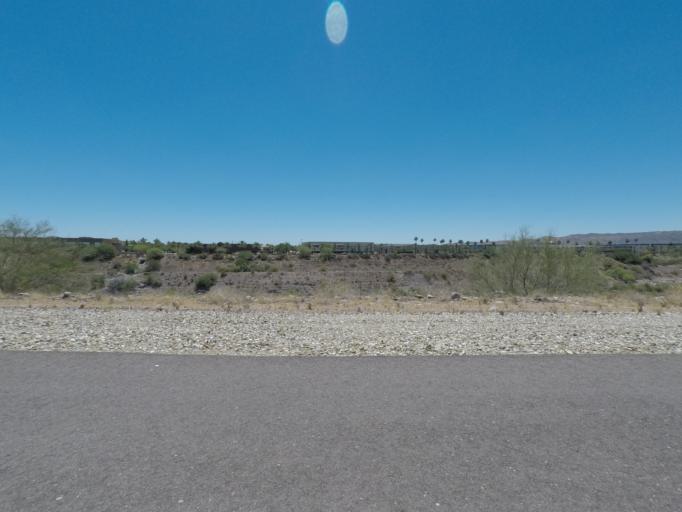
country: US
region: Arizona
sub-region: Maricopa County
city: Tempe Junction
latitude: 33.4222
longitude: -112.0094
